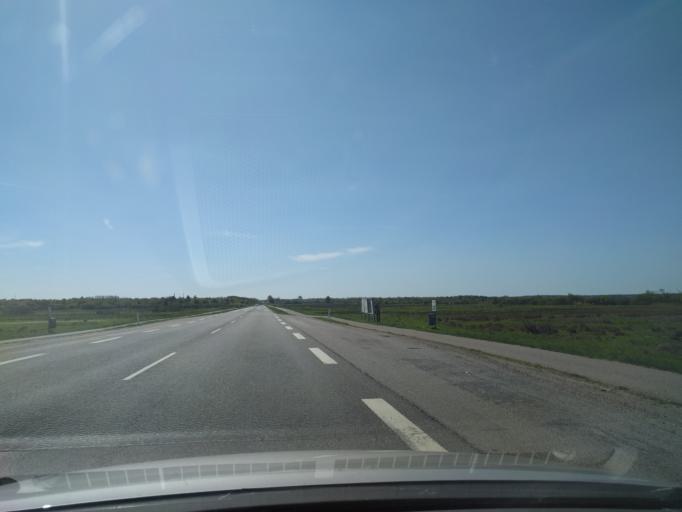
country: DK
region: Central Jutland
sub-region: Ringkobing-Skjern Kommune
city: Skjern
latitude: 55.9286
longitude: 8.5128
